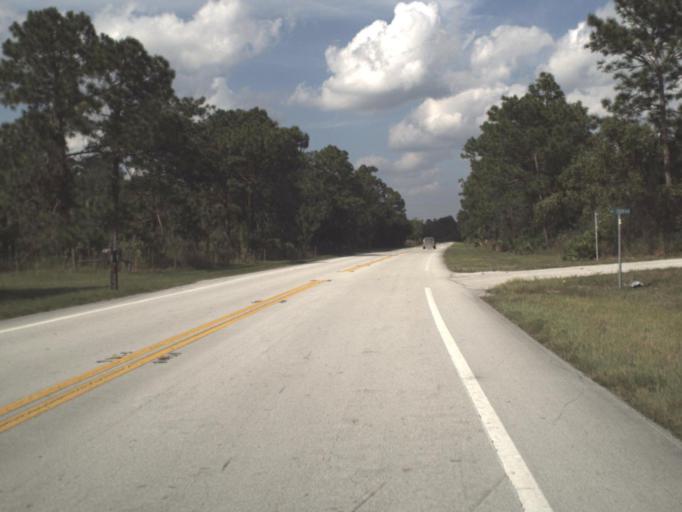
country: US
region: Florida
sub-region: Indian River County
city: Fellsmere
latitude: 27.5738
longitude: -80.8332
